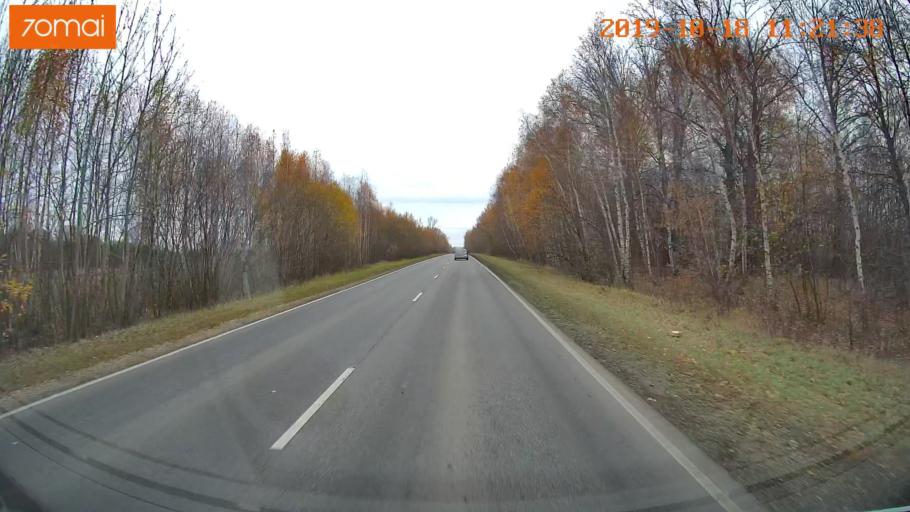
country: RU
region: Tula
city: Kimovsk
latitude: 54.0766
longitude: 38.5681
